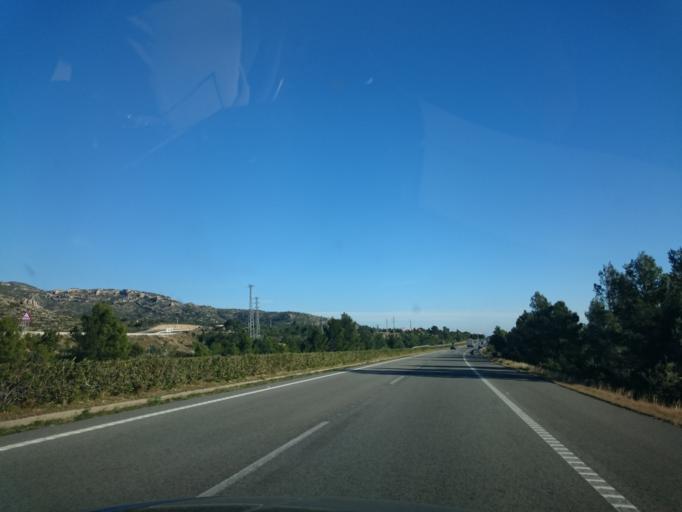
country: ES
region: Catalonia
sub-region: Provincia de Tarragona
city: Colldejou
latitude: 40.9810
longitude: 0.8871
